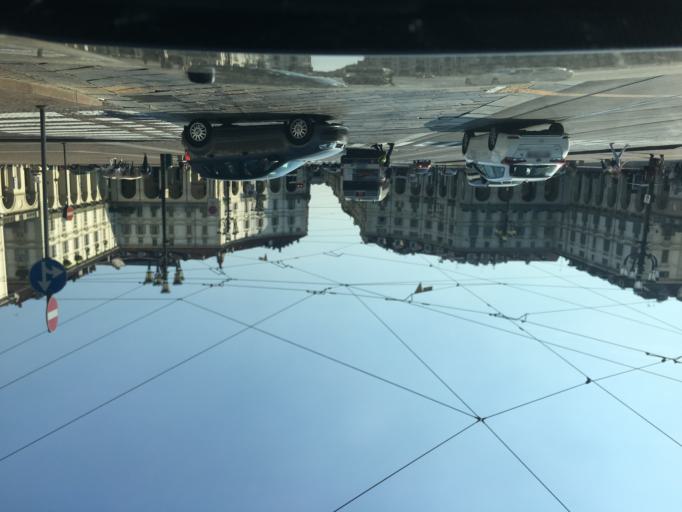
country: IT
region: Piedmont
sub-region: Provincia di Torino
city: Turin
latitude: 45.0651
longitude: 7.6951
